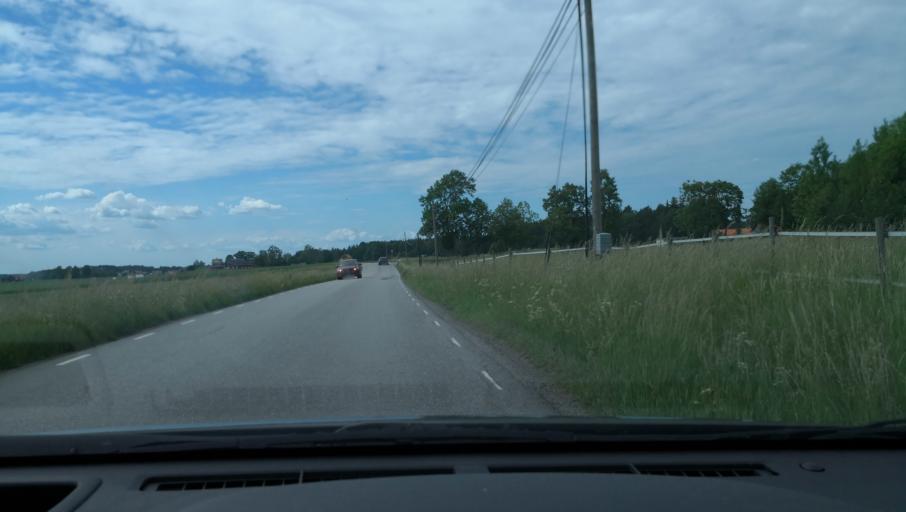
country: SE
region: Uppsala
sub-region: Uppsala Kommun
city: Uppsala
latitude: 59.8053
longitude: 17.5326
